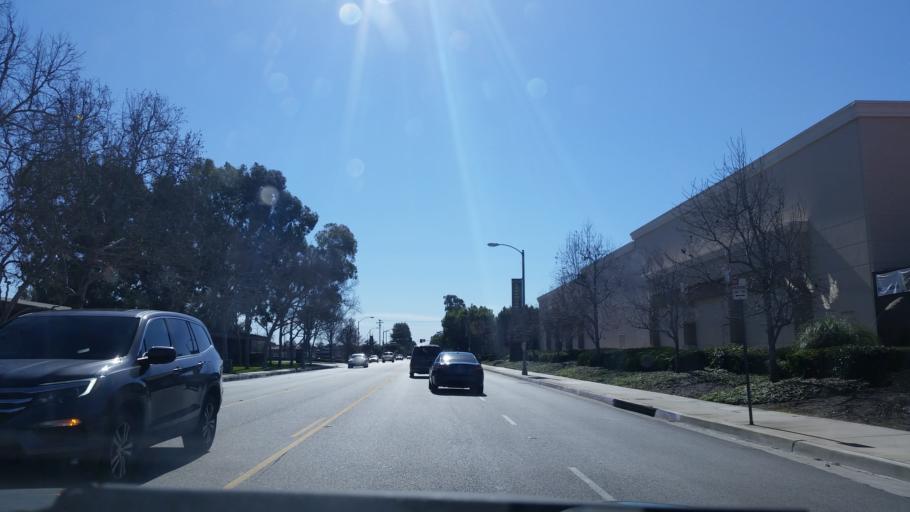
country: US
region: California
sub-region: Los Angeles County
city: Lakewood
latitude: 33.8496
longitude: -118.1338
